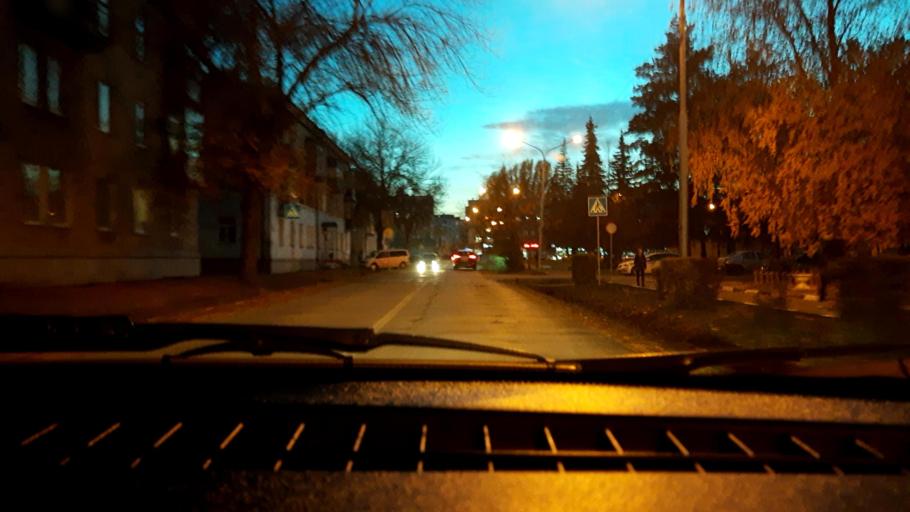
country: RU
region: Bashkortostan
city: Mikhaylovka
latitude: 54.7056
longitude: 55.8375
